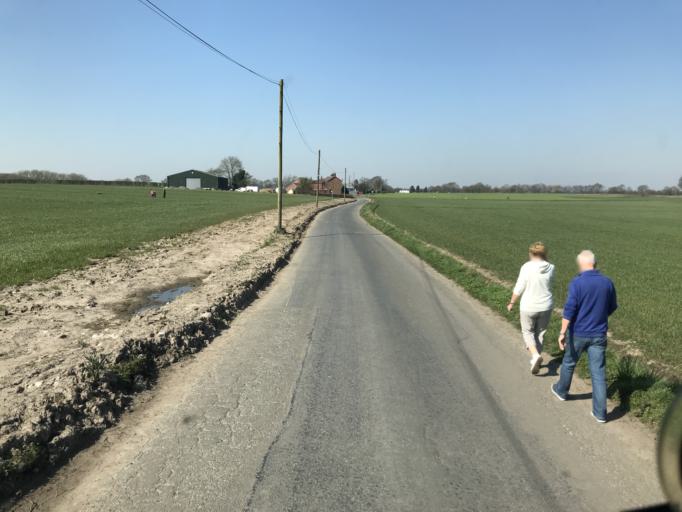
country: GB
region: England
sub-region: Trafford
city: Partington
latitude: 53.4214
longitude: -2.4653
